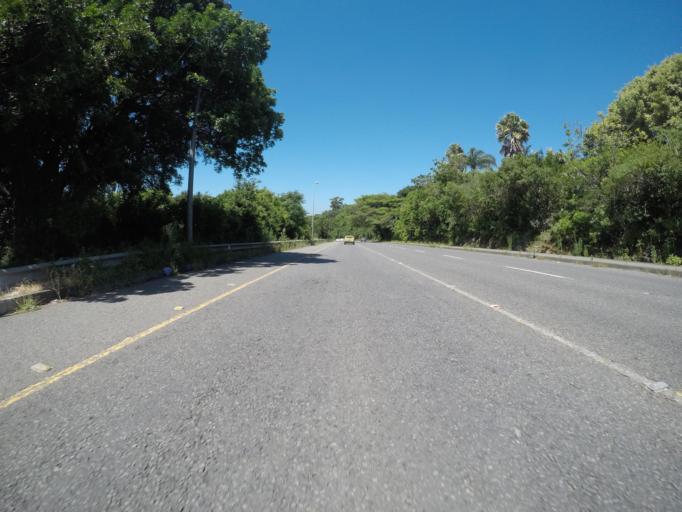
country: ZA
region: Eastern Cape
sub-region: Buffalo City Metropolitan Municipality
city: East London
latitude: -32.9671
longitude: 27.9312
